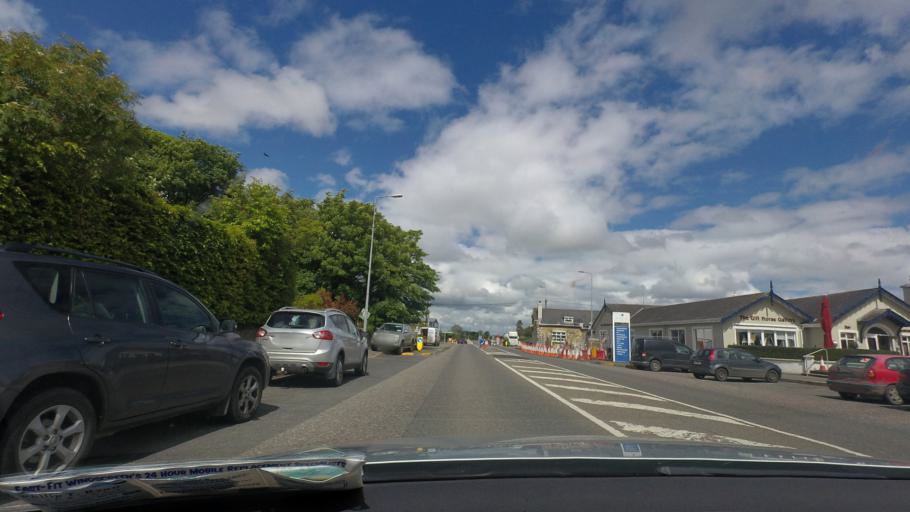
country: IE
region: Munster
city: Thurles
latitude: 52.6155
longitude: -7.7765
